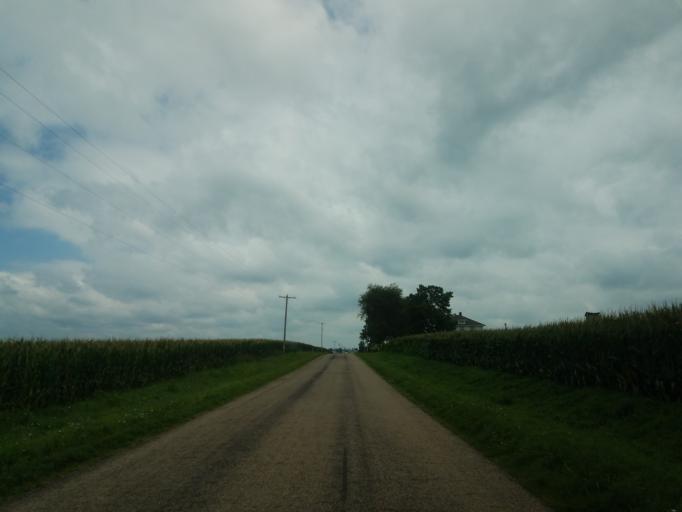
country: US
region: Illinois
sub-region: McLean County
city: Twin Grove
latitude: 40.4240
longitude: -89.0622
